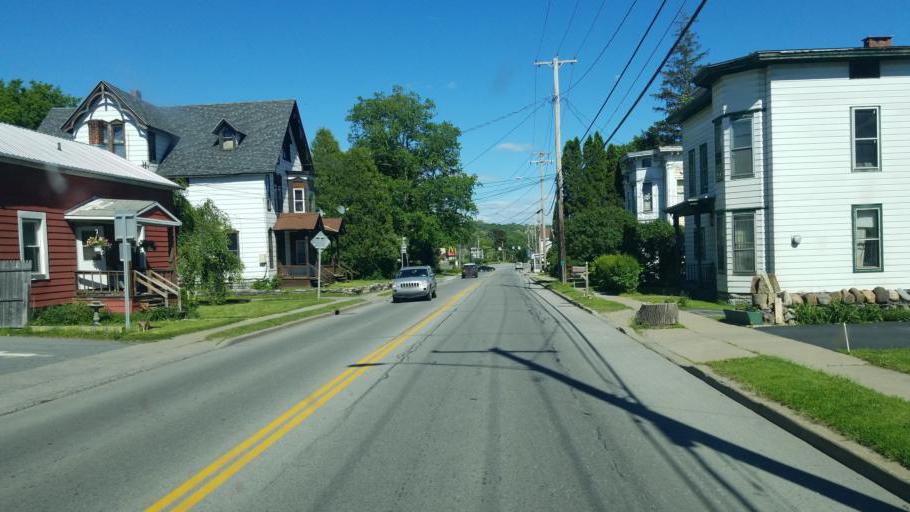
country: US
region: New York
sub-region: Montgomery County
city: Canajoharie
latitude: 42.9111
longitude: -74.5738
